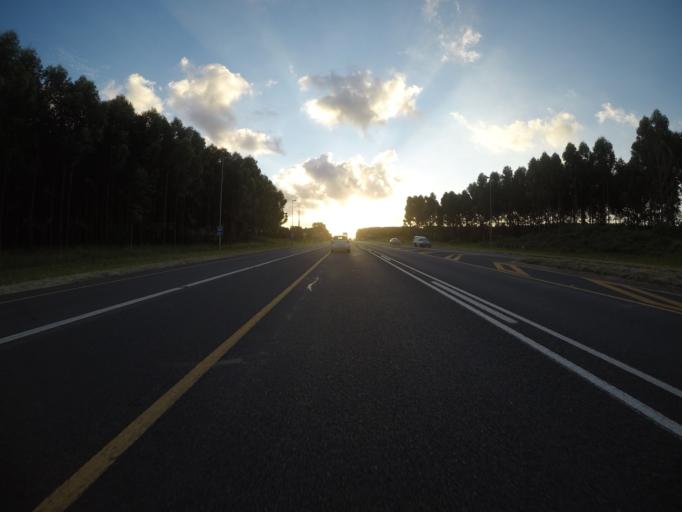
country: ZA
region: KwaZulu-Natal
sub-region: uThungulu District Municipality
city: Richards Bay
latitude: -28.6947
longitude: 32.0258
